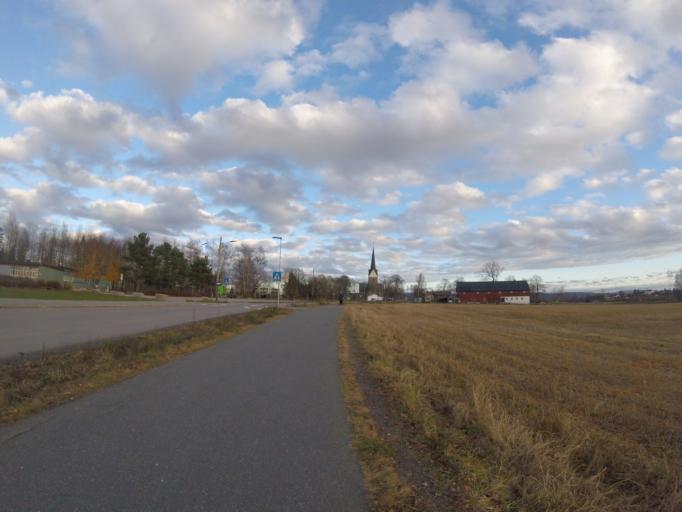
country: NO
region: Akershus
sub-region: Skedsmo
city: Lillestrom
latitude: 59.9938
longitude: 11.0405
